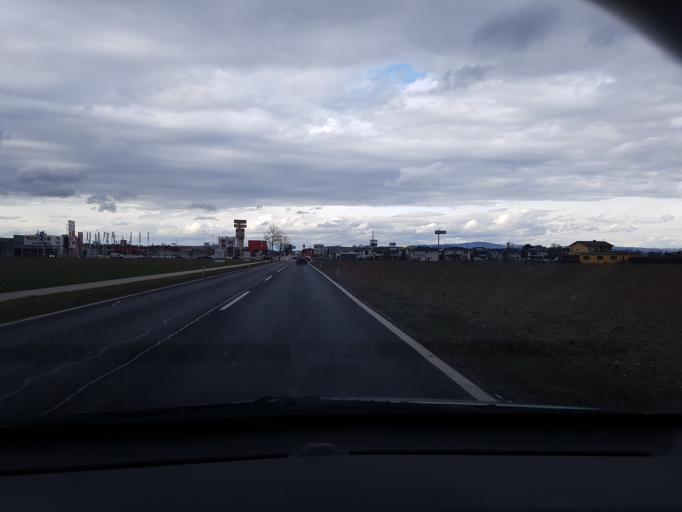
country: AT
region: Upper Austria
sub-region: Politischer Bezirk Linz-Land
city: Traun
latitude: 48.1923
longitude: 14.2514
